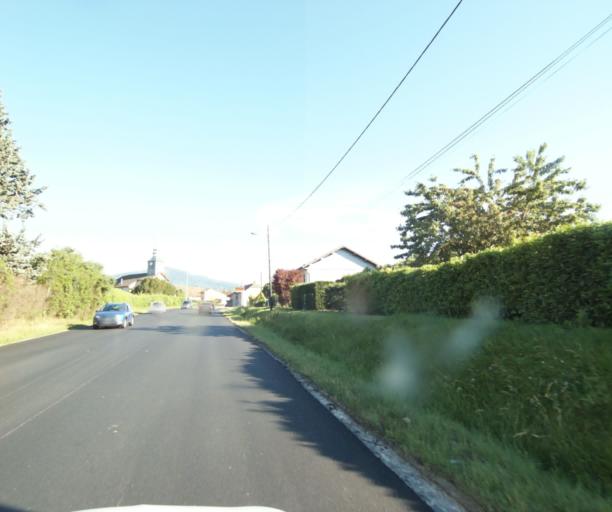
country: FR
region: Rhone-Alpes
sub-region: Departement de la Haute-Savoie
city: Loisin
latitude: 46.2932
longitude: 6.3093
